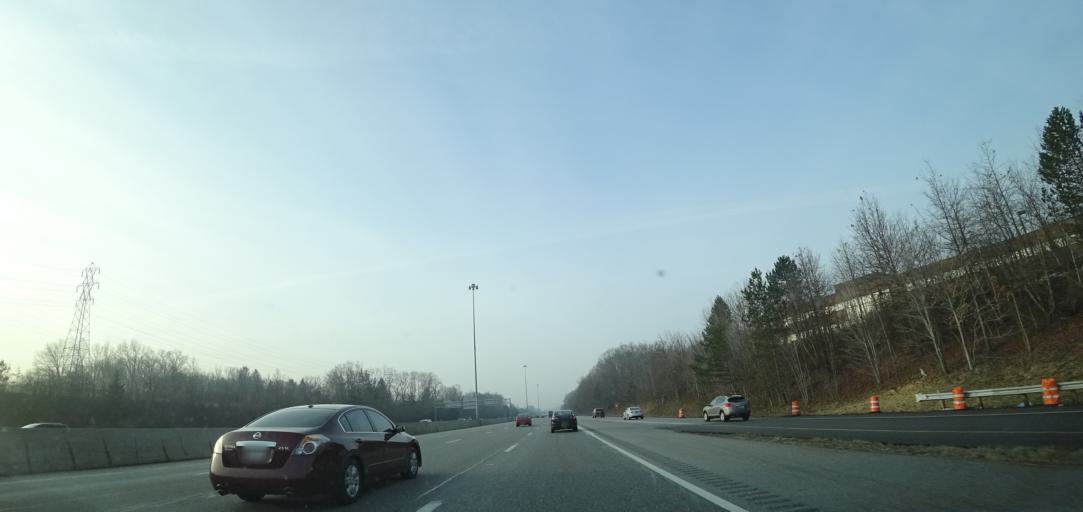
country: US
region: Ohio
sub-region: Cuyahoga County
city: Seven Hills
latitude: 41.3941
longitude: -81.6532
